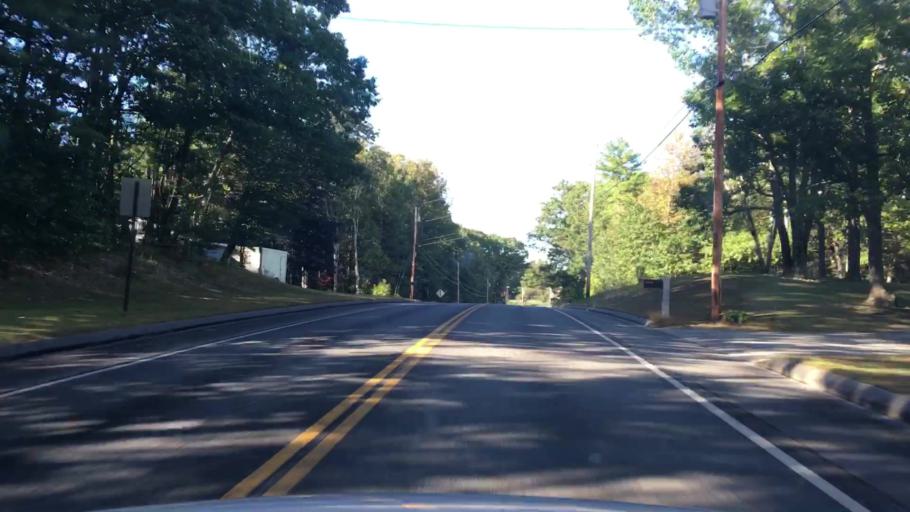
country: US
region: Maine
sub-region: Androscoggin County
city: Lisbon Falls
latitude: 44.0092
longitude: -70.0696
